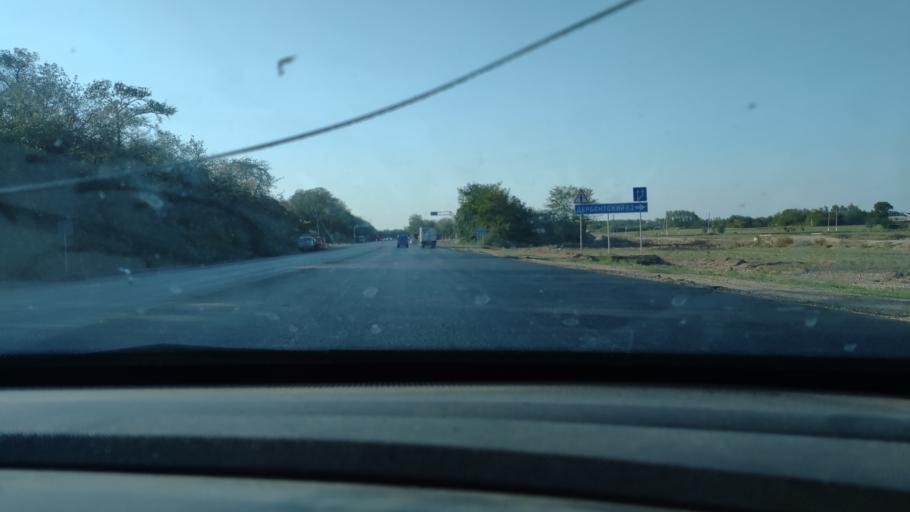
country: RU
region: Krasnodarskiy
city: Medvedovskaya
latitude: 45.4972
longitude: 38.9498
